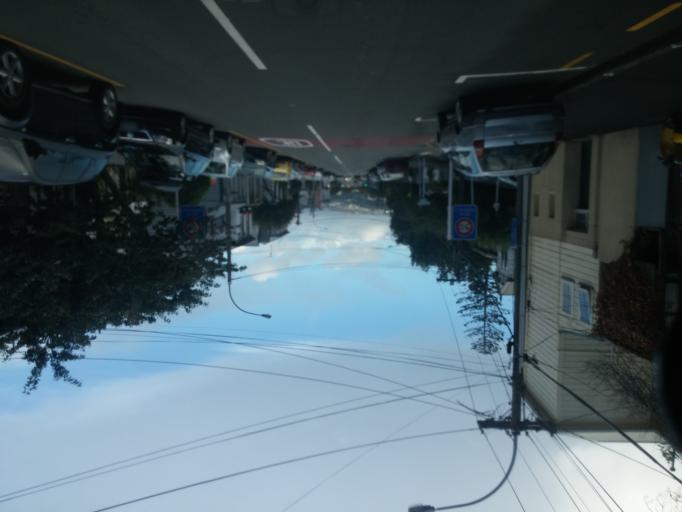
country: NZ
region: Wellington
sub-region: Wellington City
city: Kelburn
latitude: -41.2777
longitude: 174.7704
